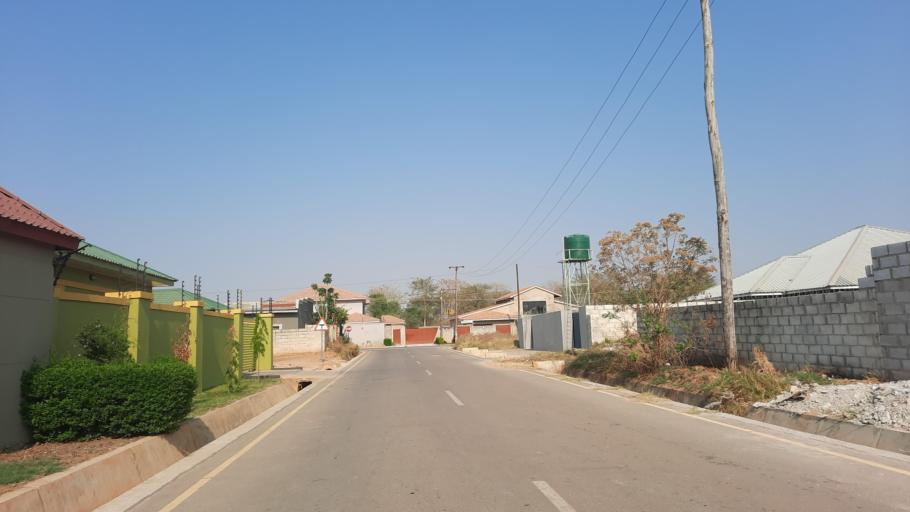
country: ZM
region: Lusaka
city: Lusaka
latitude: -15.3915
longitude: 28.3859
